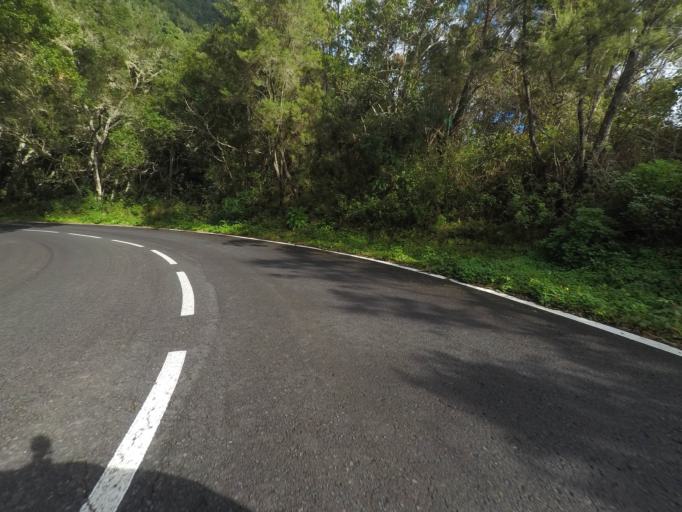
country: ES
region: Canary Islands
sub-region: Provincia de Santa Cruz de Tenerife
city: Hermigua
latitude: 28.1284
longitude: -17.2110
